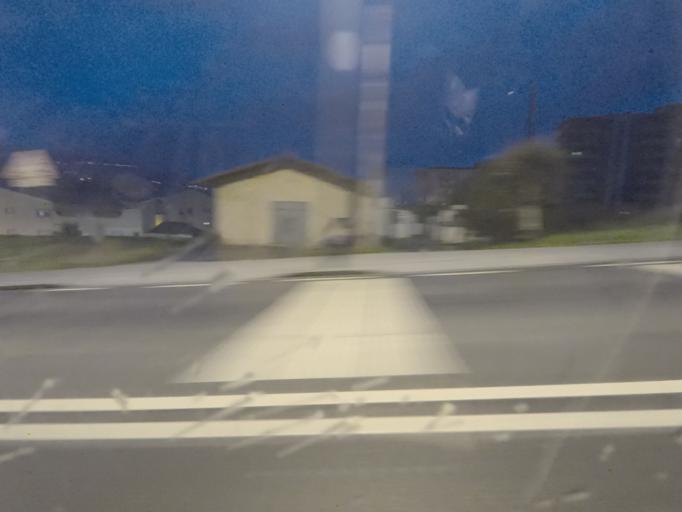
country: PT
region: Vila Real
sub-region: Peso da Regua
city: Peso da Regua
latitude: 41.1565
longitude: -7.7771
